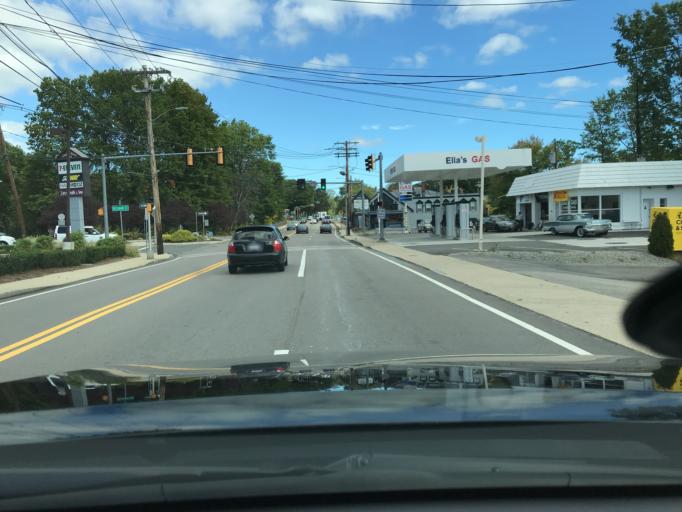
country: US
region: Massachusetts
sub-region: Norfolk County
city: Dedham
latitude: 42.2697
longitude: -71.1744
